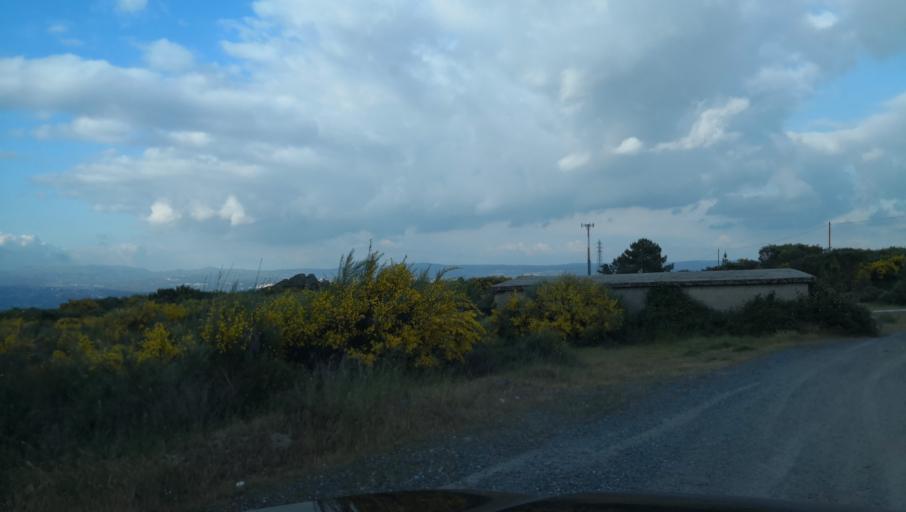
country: PT
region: Vila Real
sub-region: Vila Real
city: Vila Real
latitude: 41.2733
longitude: -7.7842
